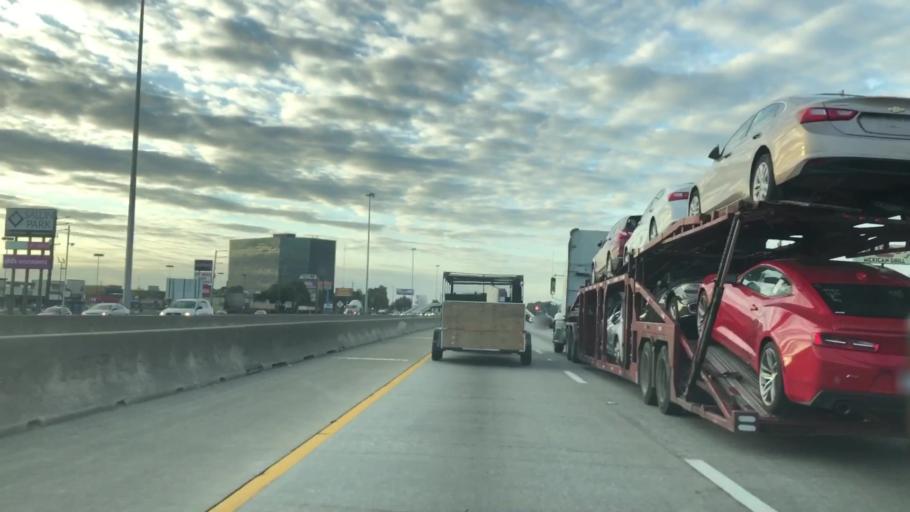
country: US
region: Texas
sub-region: Harris County
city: Aldine
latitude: 29.9248
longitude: -95.4122
